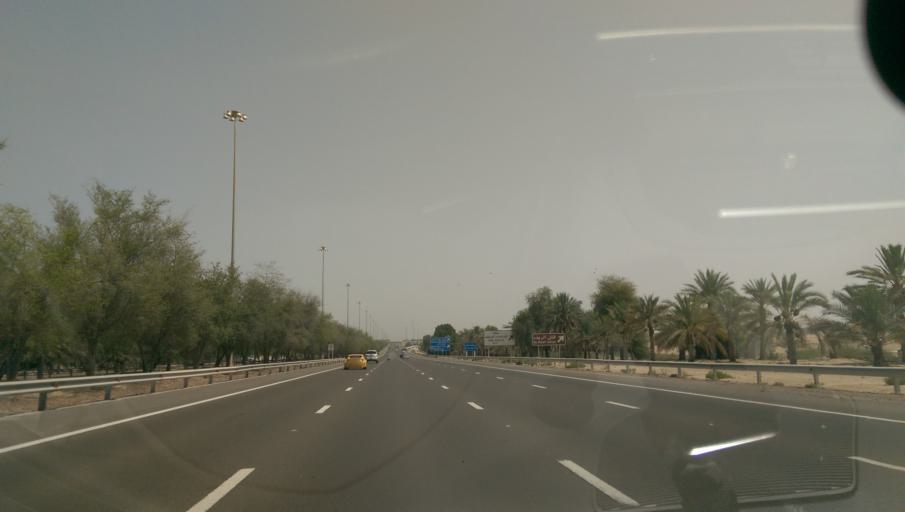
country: AE
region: Abu Dhabi
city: Abu Dhabi
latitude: 24.4555
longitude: 54.6785
